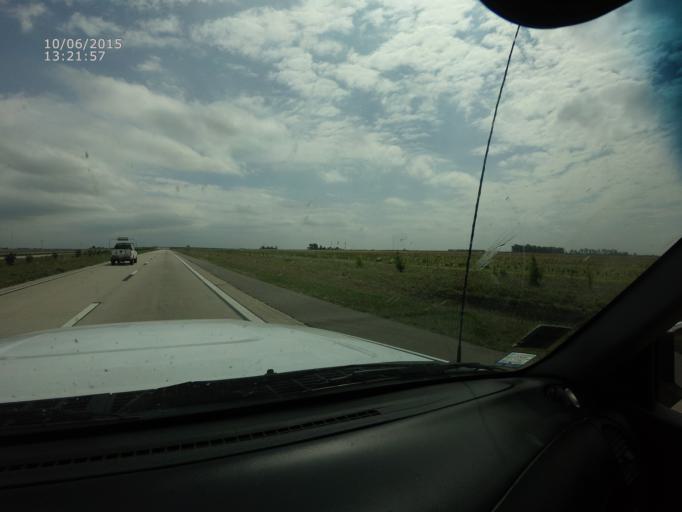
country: AR
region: Cordoba
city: Marcos Juarez
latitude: -32.6664
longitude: -62.0851
